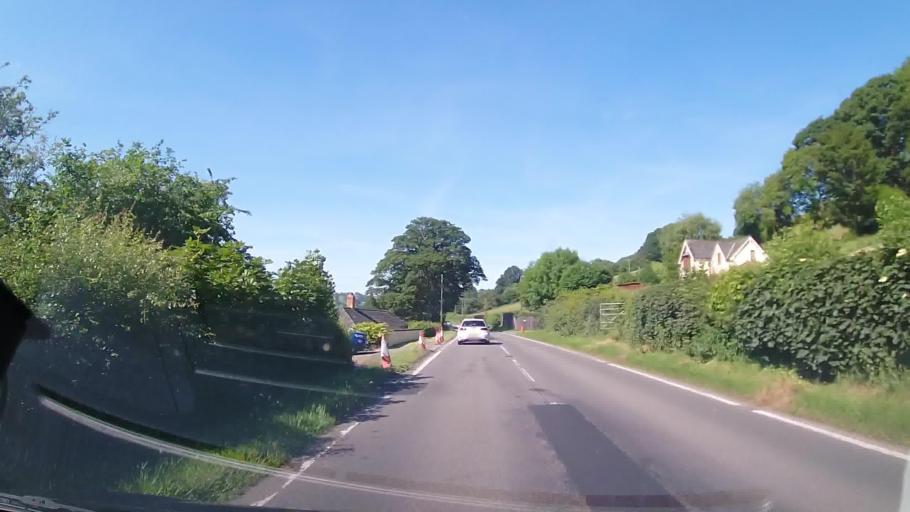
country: GB
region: Wales
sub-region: Sir Powys
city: Llanfyllin
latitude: 52.6595
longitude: -3.3115
